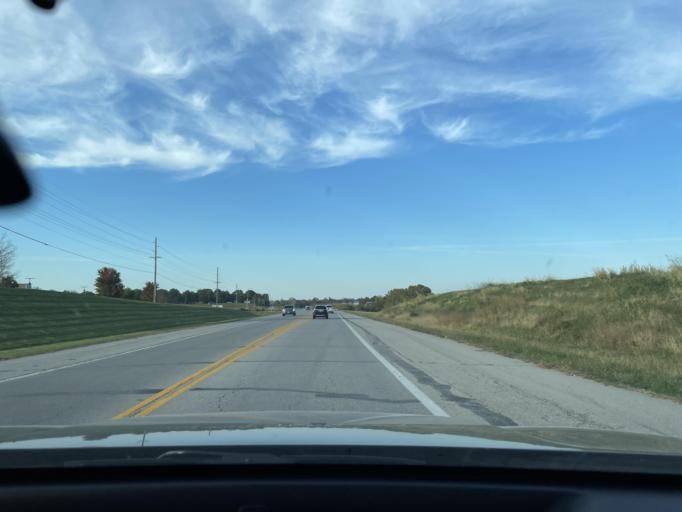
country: US
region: Missouri
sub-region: Buchanan County
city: Saint Joseph
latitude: 39.7725
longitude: -94.7681
